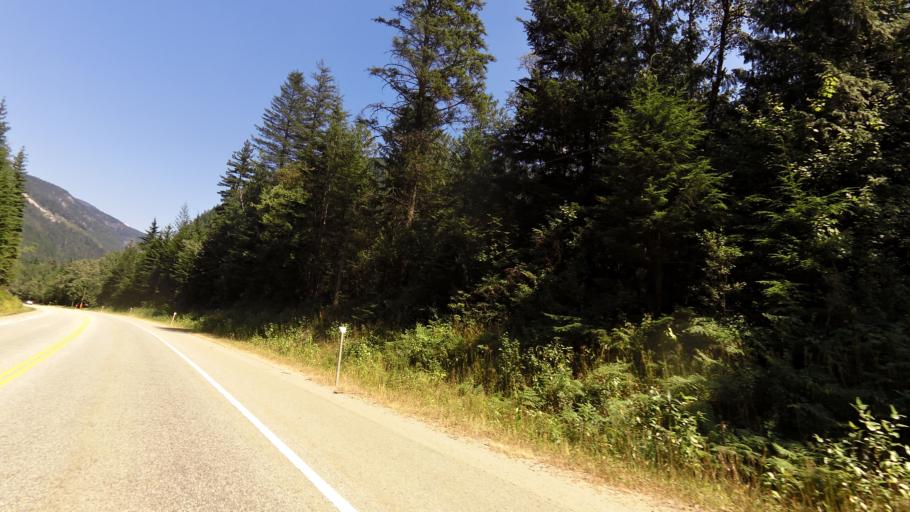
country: CA
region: British Columbia
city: Revelstoke
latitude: 50.9498
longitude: -118.4086
